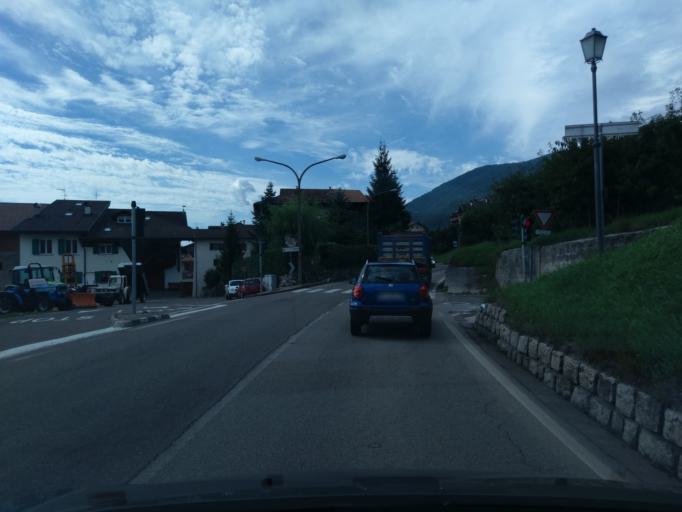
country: IT
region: Trentino-Alto Adige
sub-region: Provincia di Trento
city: Cles
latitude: 46.3741
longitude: 11.0336
